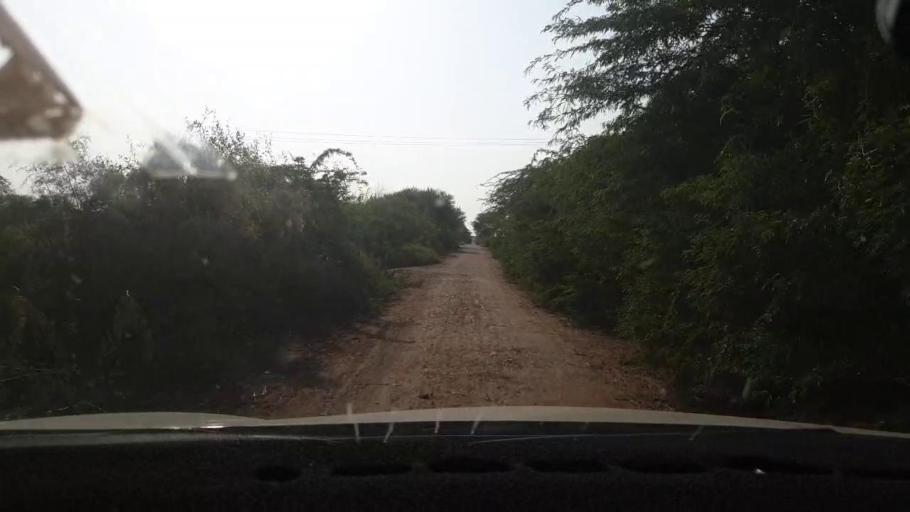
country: PK
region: Sindh
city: Berani
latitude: 25.7488
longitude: 68.7800
